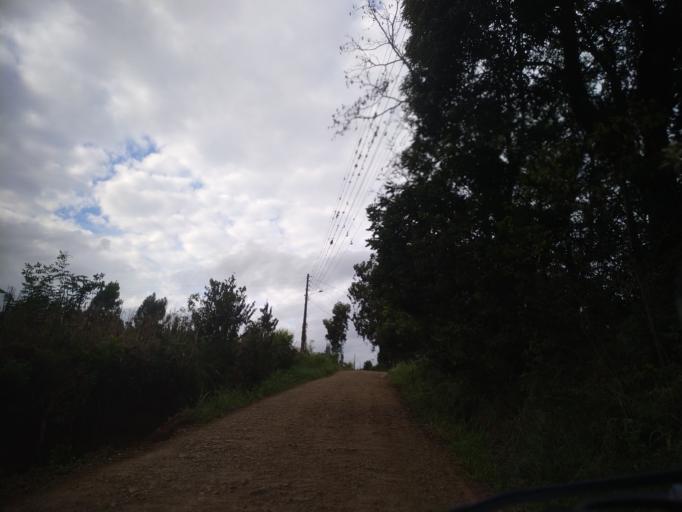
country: BR
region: Santa Catarina
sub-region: Chapeco
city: Chapeco
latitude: -27.0673
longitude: -52.6122
